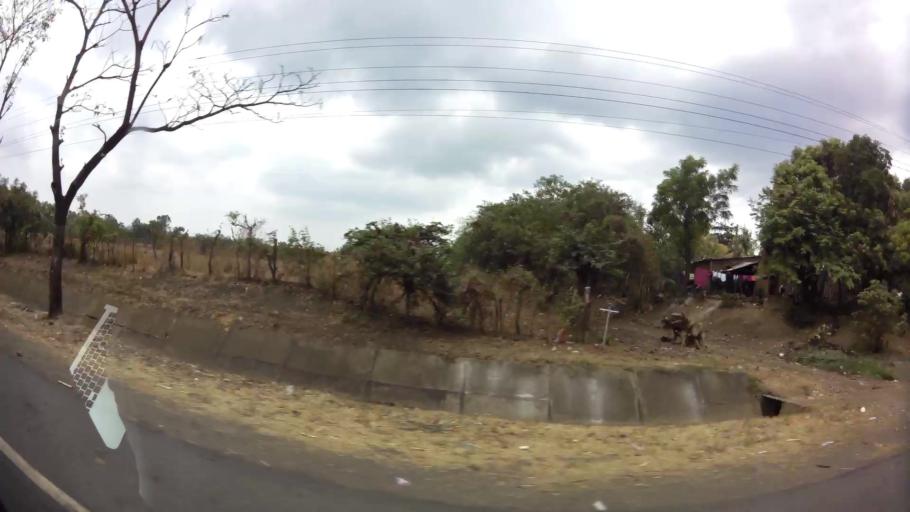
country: NI
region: Leon
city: Telica
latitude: 12.4801
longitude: -86.8623
